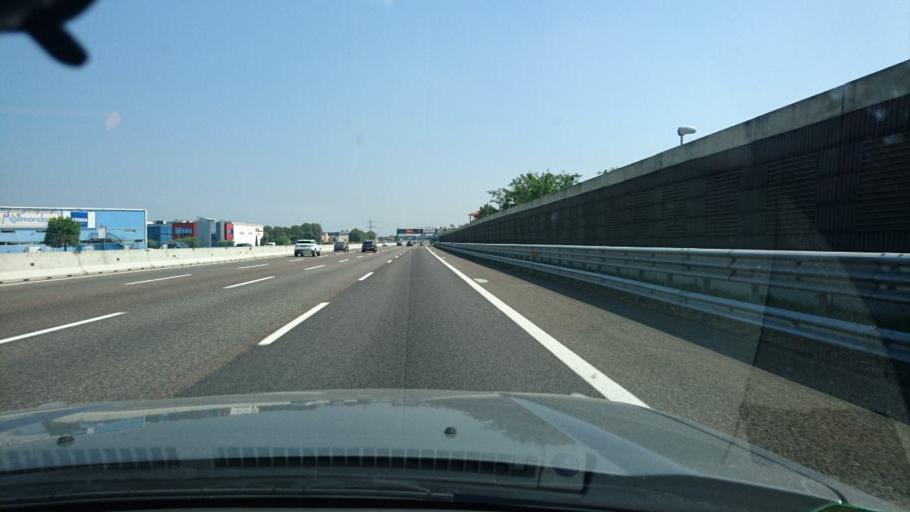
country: IT
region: Lombardy
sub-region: Provincia di Bergamo
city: Osio Sopra
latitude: 45.6192
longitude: 9.5715
